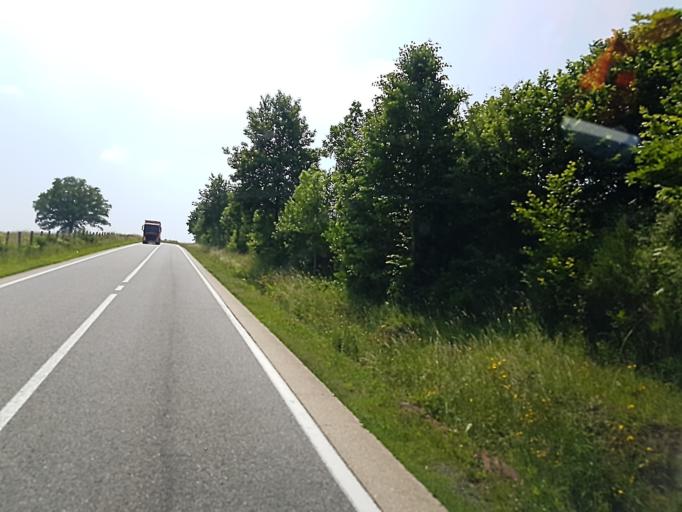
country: BE
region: Wallonia
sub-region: Province de Liege
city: Trois-Ponts
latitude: 50.3523
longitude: 5.8225
